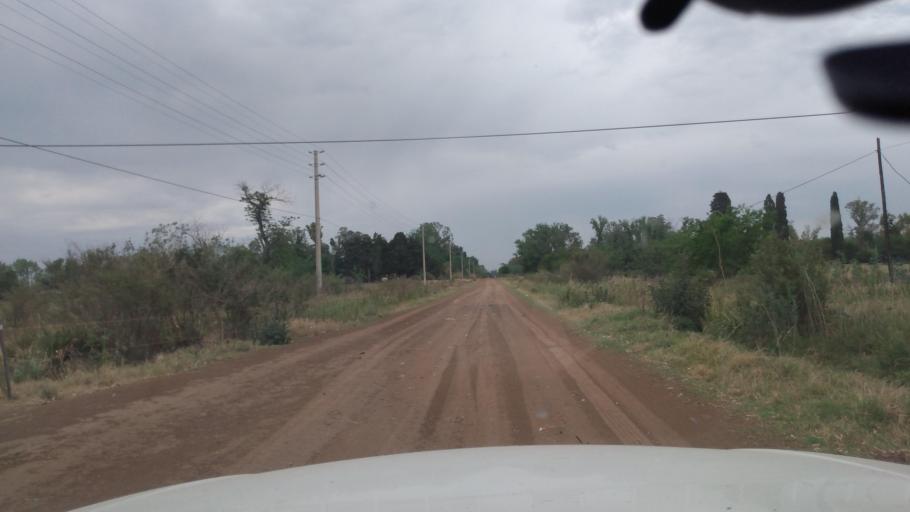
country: AR
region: Buenos Aires
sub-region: Partido de Lujan
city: Lujan
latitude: -34.5550
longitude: -59.1770
